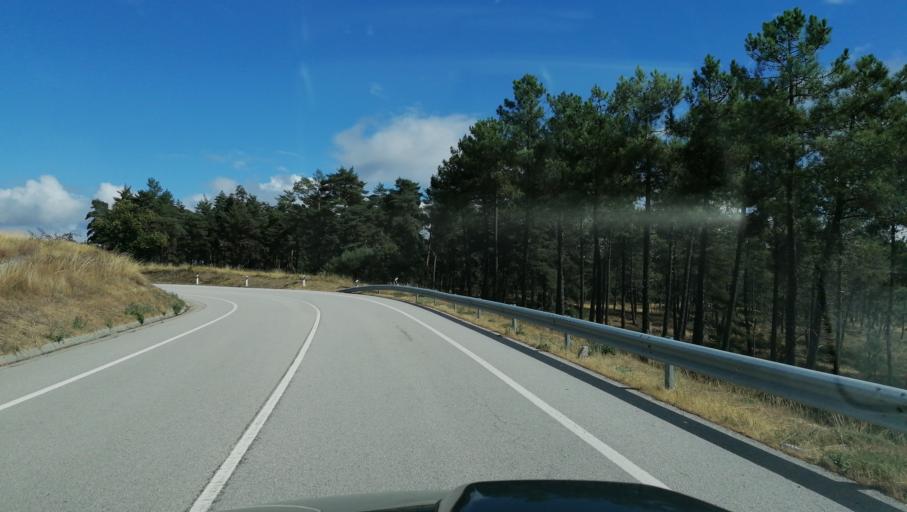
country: PT
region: Vila Real
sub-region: Vila Pouca de Aguiar
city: Vila Pouca de Aguiar
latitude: 41.5197
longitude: -7.5945
